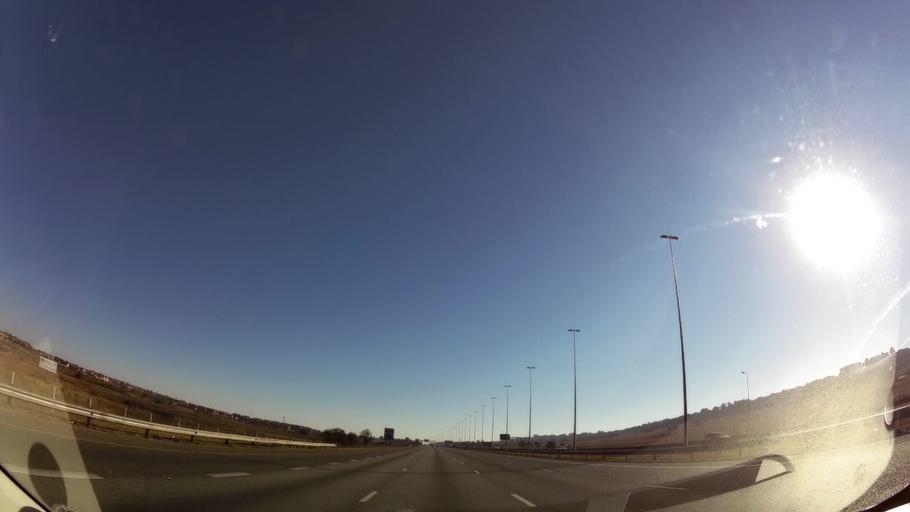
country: ZA
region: Gauteng
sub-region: City of Tshwane Metropolitan Municipality
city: Centurion
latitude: -25.8589
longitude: 28.2527
